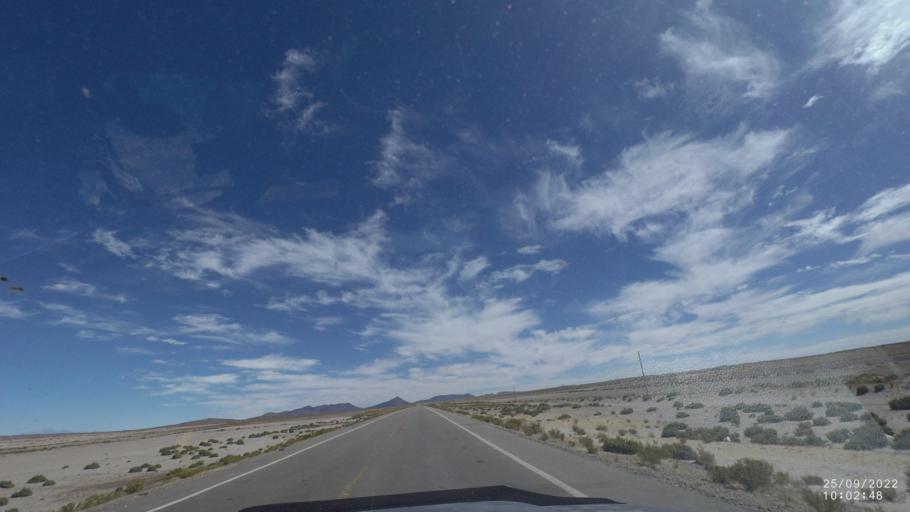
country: BO
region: Potosi
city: Colchani
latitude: -20.2301
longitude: -66.9536
